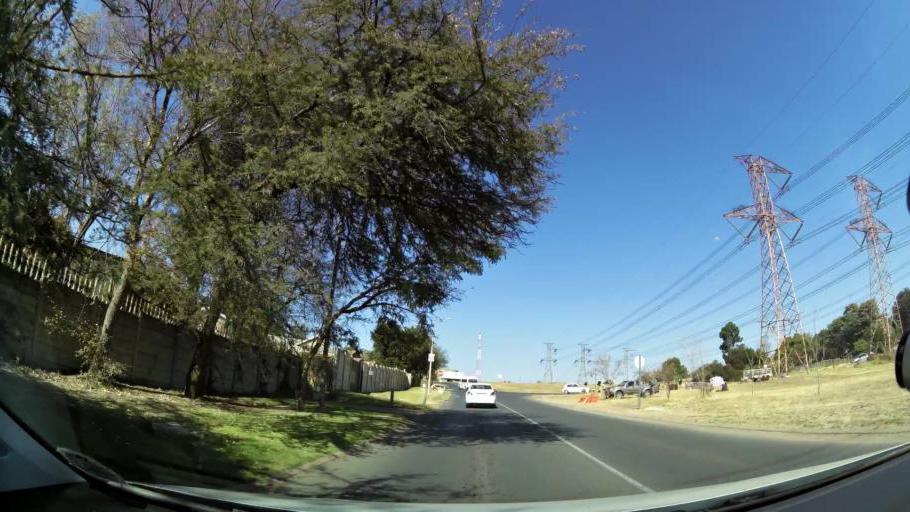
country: ZA
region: Gauteng
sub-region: City of Johannesburg Metropolitan Municipality
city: Modderfontein
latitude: -26.0605
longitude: 28.2152
